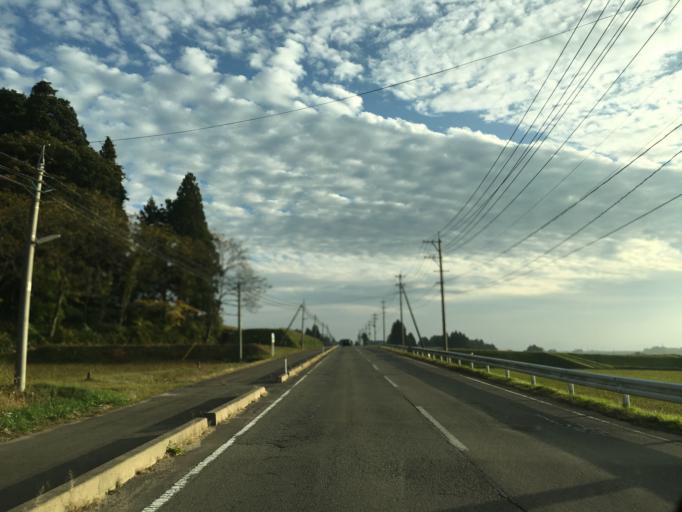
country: JP
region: Fukushima
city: Inawashiro
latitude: 37.5528
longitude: 140.1406
